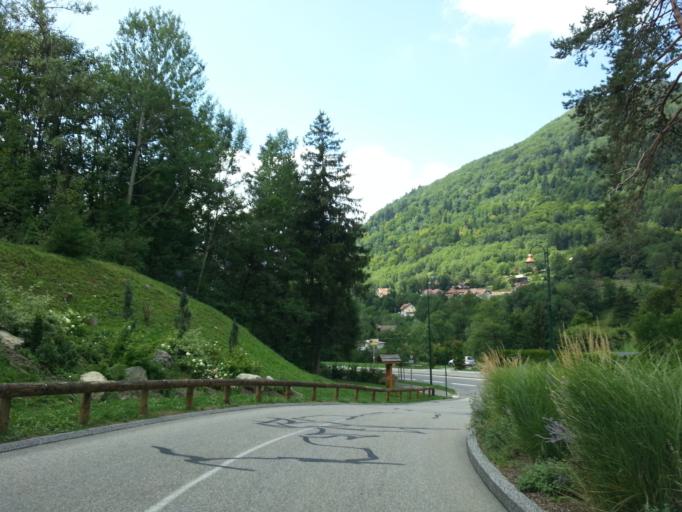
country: FR
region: Rhone-Alpes
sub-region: Departement de la Haute-Savoie
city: Menthon-Saint-Bernard
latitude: 45.8745
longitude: 6.2140
